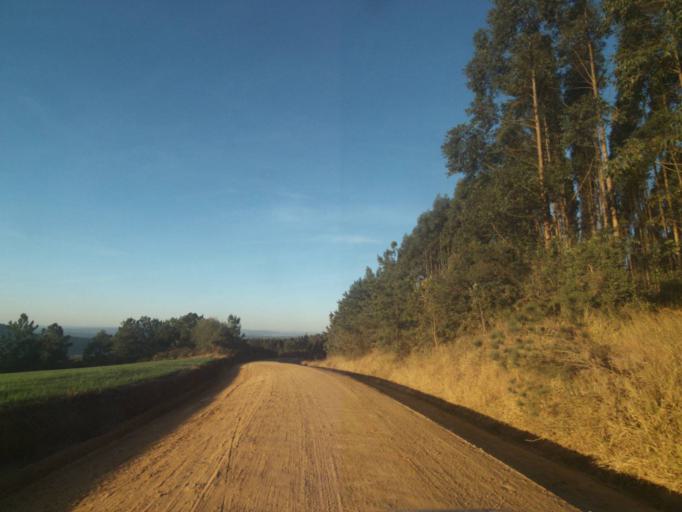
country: BR
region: Parana
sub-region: Tibagi
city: Tibagi
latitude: -24.5476
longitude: -50.5349
